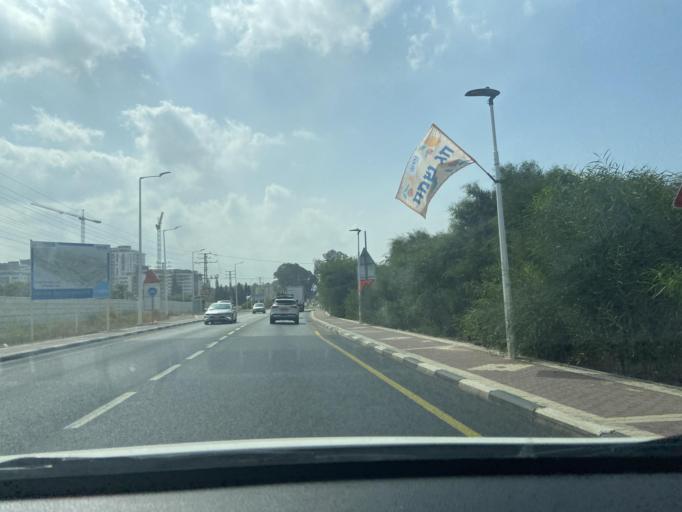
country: IL
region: Northern District
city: Nahariya
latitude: 33.0203
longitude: 35.1037
